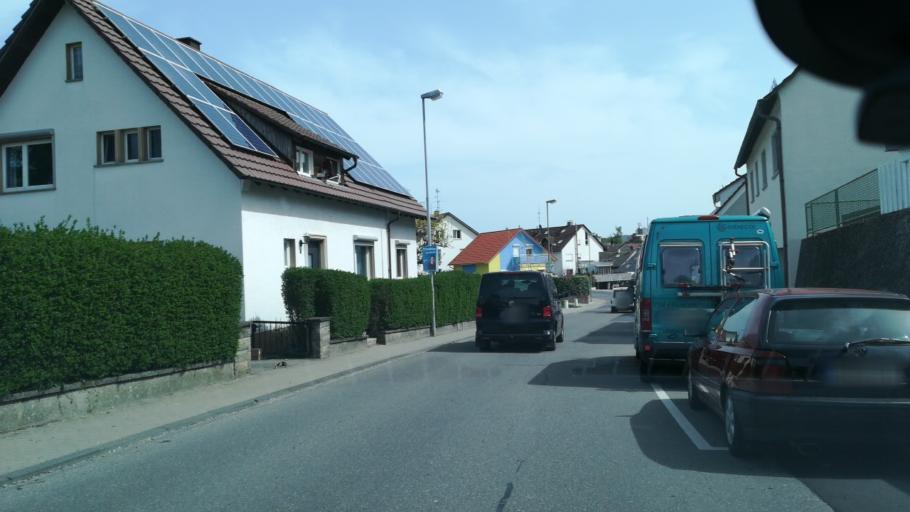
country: DE
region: Baden-Wuerttemberg
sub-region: Freiburg Region
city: Allensbach
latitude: 47.7381
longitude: 9.1138
